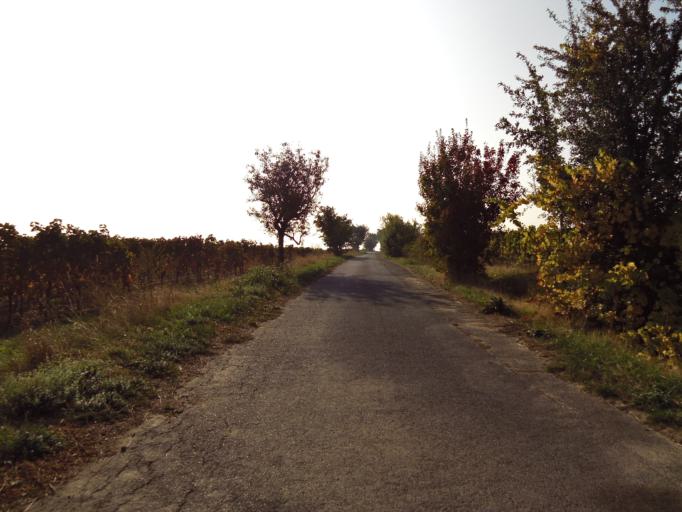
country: DE
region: Rheinland-Pfalz
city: Kindenheim
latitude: 49.6095
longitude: 8.1716
